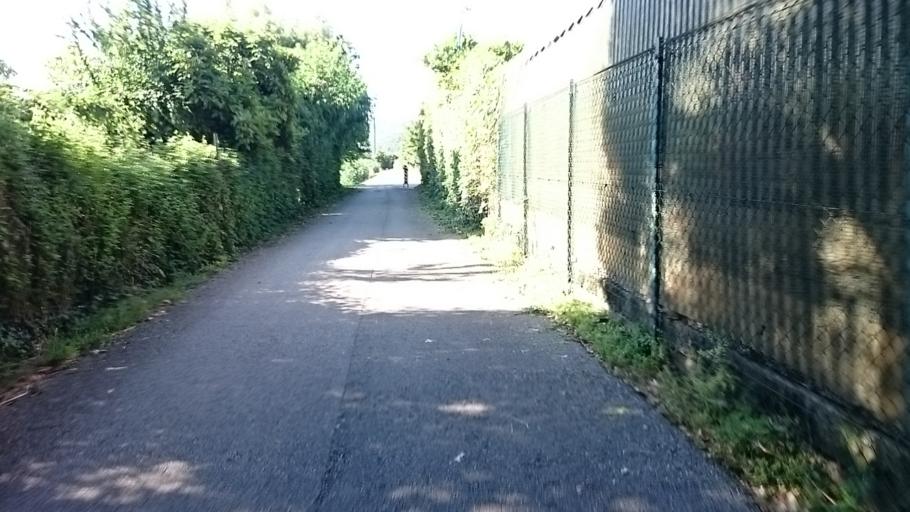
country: IT
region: Veneto
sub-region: Provincia di Vicenza
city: Arcugnano-Torri
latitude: 45.5143
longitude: 11.5682
